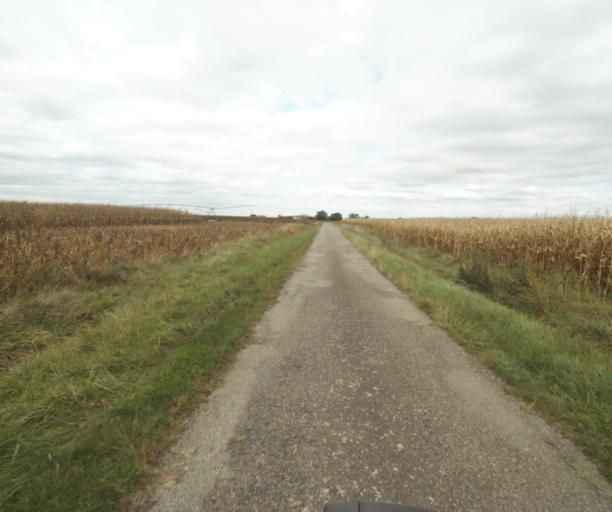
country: FR
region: Midi-Pyrenees
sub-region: Departement du Tarn-et-Garonne
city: Verdun-sur-Garonne
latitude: 43.8655
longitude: 1.1531
